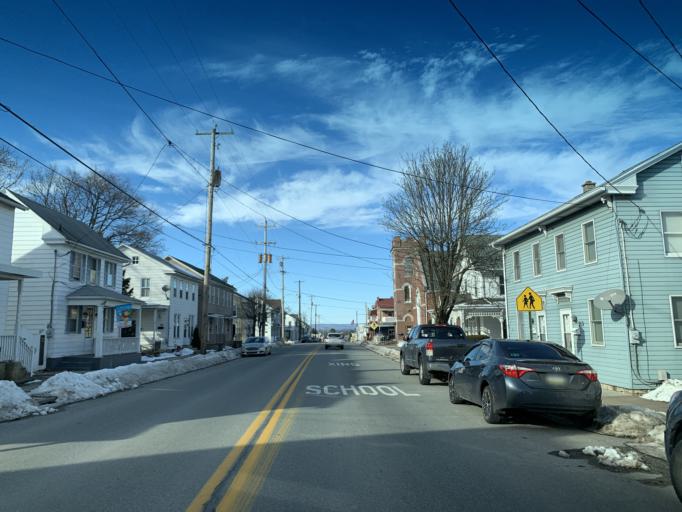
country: US
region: Pennsylvania
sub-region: York County
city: Dillsburg
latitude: 40.1066
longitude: -77.0345
